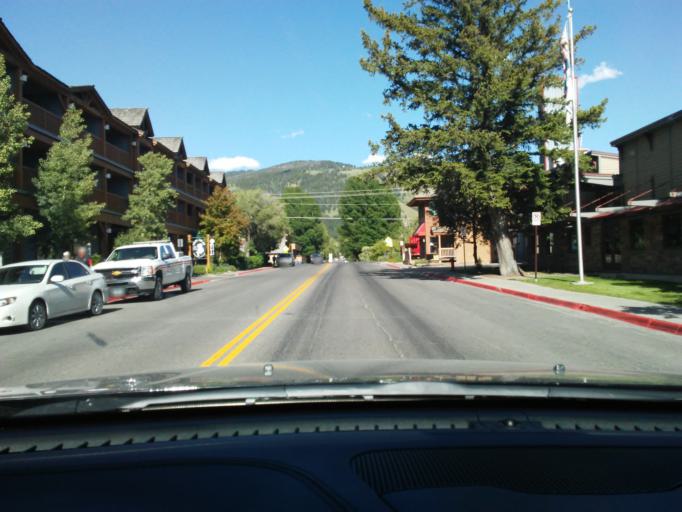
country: US
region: Wyoming
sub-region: Teton County
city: Jackson
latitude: 43.4785
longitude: -110.7617
